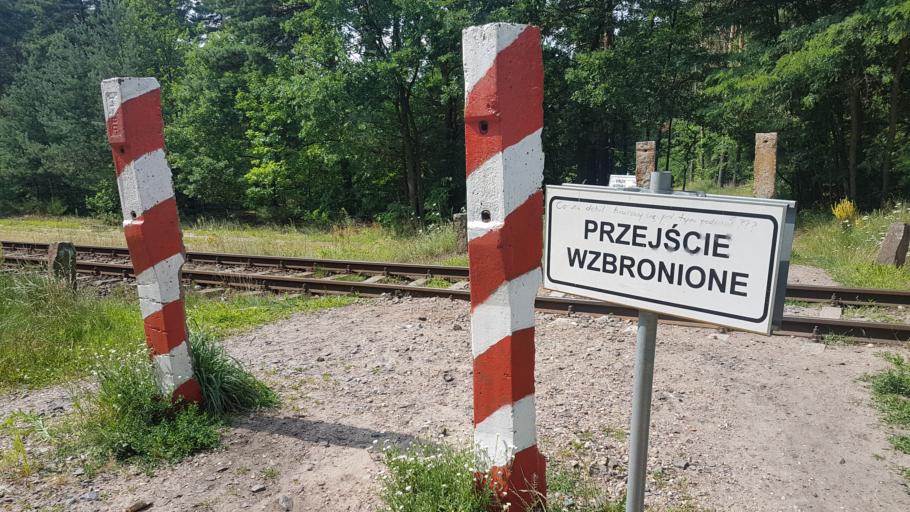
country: PL
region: Lubusz
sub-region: Zielona Gora
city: Zielona Gora
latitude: 51.9458
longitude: 15.4681
